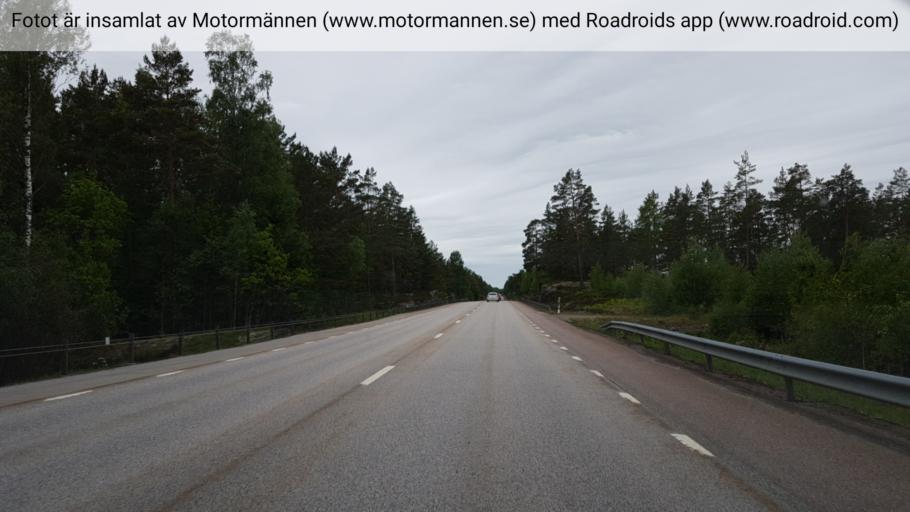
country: SE
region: Kalmar
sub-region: Oskarshamns Kommun
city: Oskarshamn
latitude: 57.4569
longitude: 16.5142
